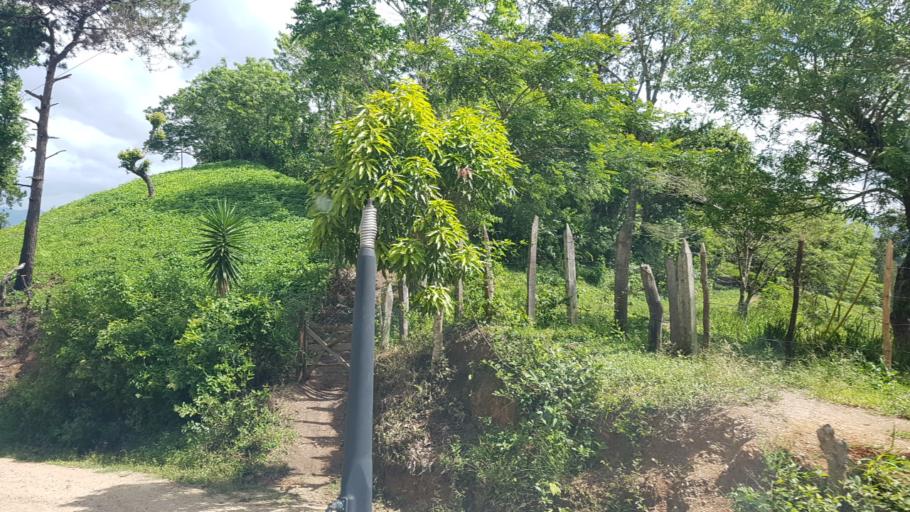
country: NI
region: Nueva Segovia
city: Ciudad Antigua
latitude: 13.6511
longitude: -86.2399
